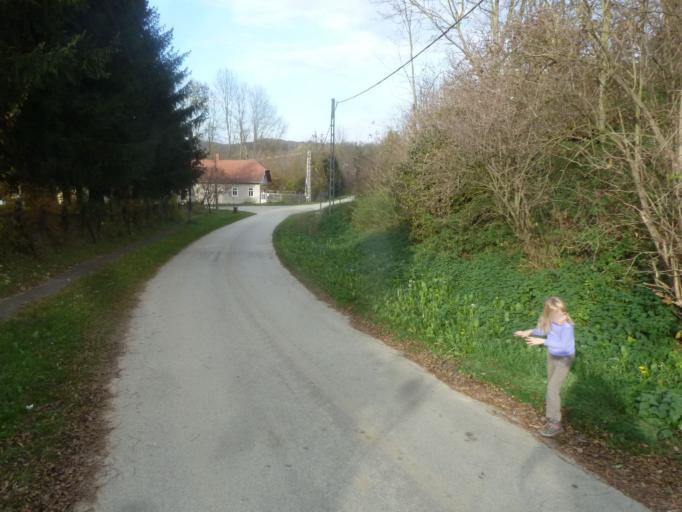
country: HU
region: Zala
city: Nagykanizsa
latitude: 46.5568
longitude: 17.0442
